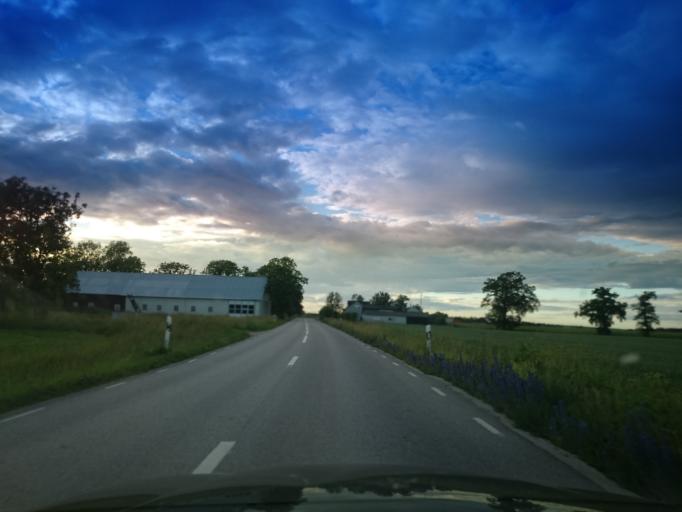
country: SE
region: Gotland
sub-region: Gotland
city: Vibble
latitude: 57.5023
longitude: 18.3723
